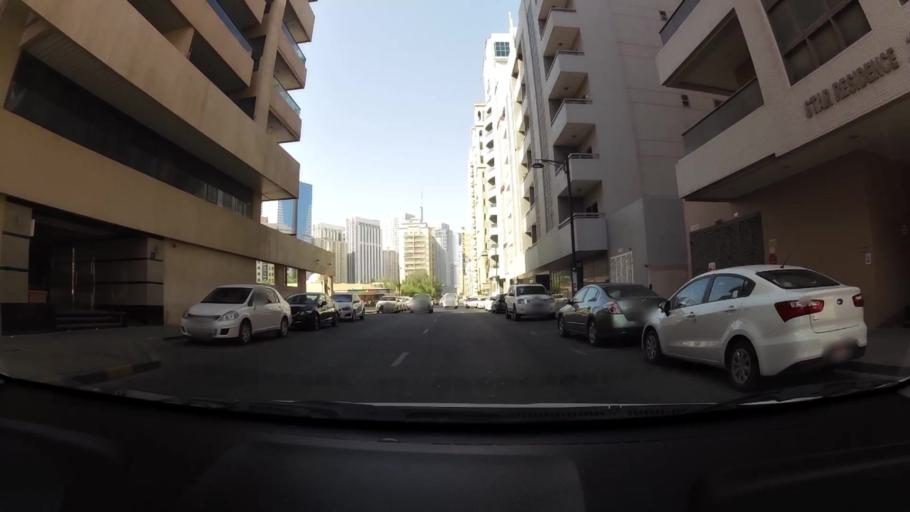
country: AE
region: Ash Shariqah
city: Sharjah
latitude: 25.2946
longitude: 55.3787
